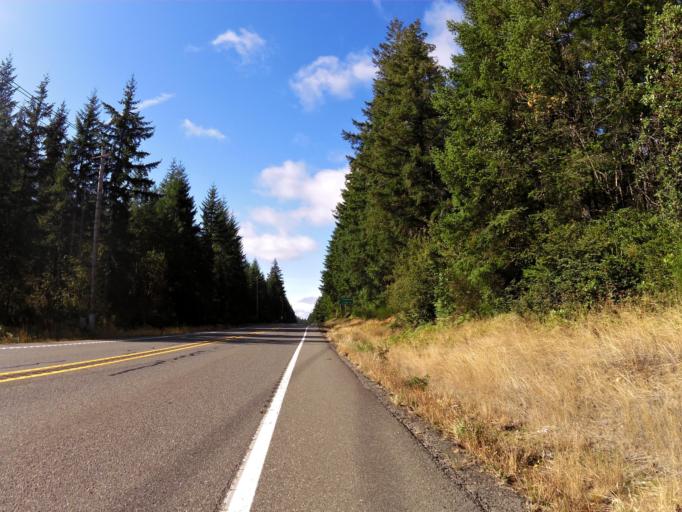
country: US
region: Washington
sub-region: Mason County
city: Allyn
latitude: 47.3184
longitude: -122.9089
